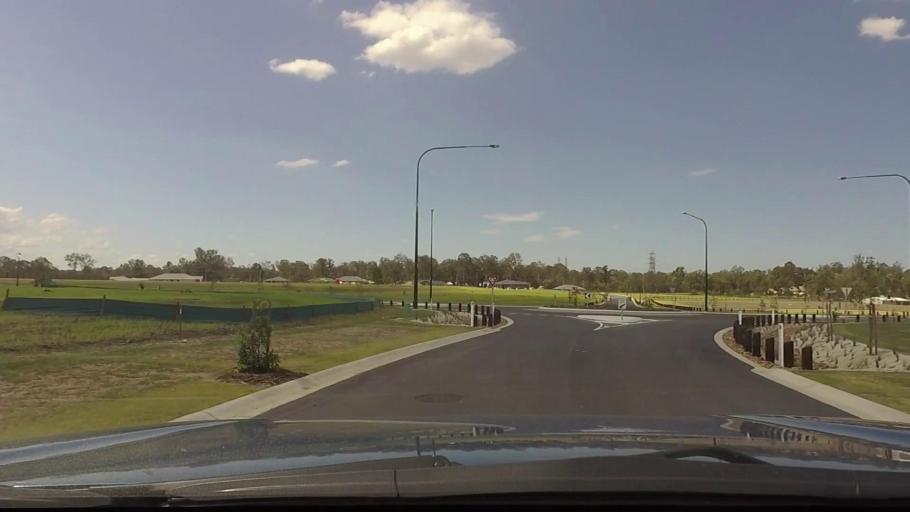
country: AU
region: Queensland
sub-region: Logan
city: North Maclean
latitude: -27.7380
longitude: 152.9509
